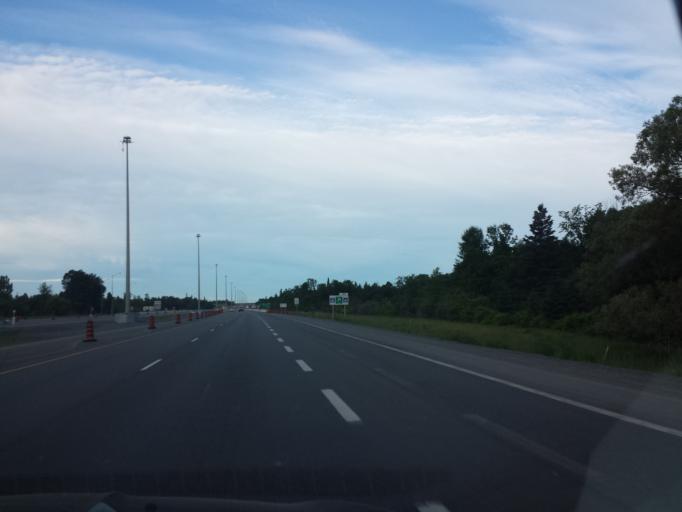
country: CA
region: Ontario
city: Bells Corners
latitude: 45.2929
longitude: -75.9389
